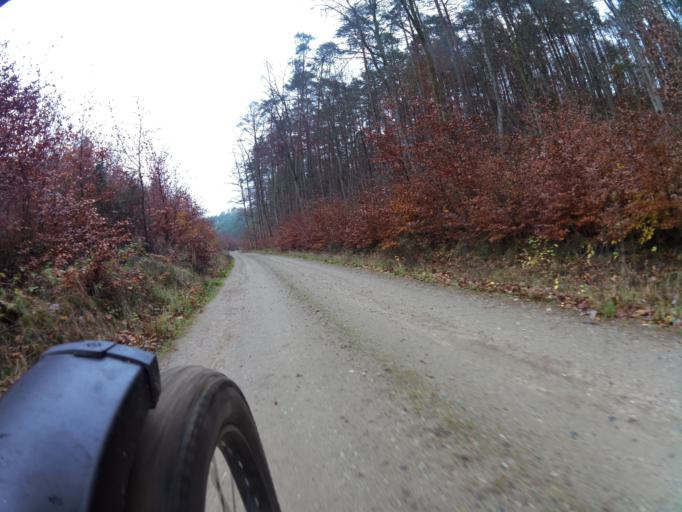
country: PL
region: Pomeranian Voivodeship
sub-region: Powiat wejherowski
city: Orle
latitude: 54.7062
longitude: 18.1461
